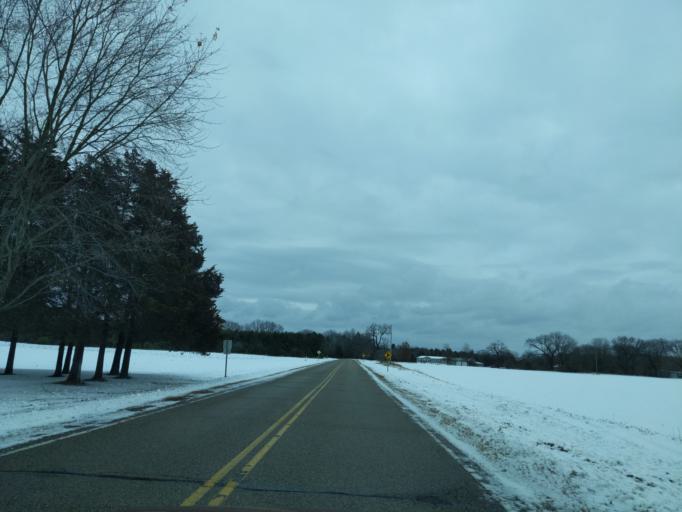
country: US
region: Wisconsin
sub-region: Marquette County
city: Westfield
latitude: 43.9088
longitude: -89.3734
